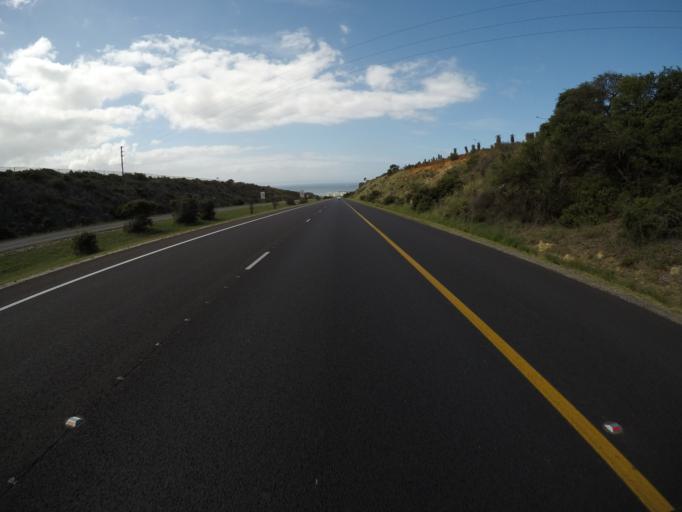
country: ZA
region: Western Cape
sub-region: Eden District Municipality
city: Mossel Bay
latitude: -34.1629
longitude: 22.0925
